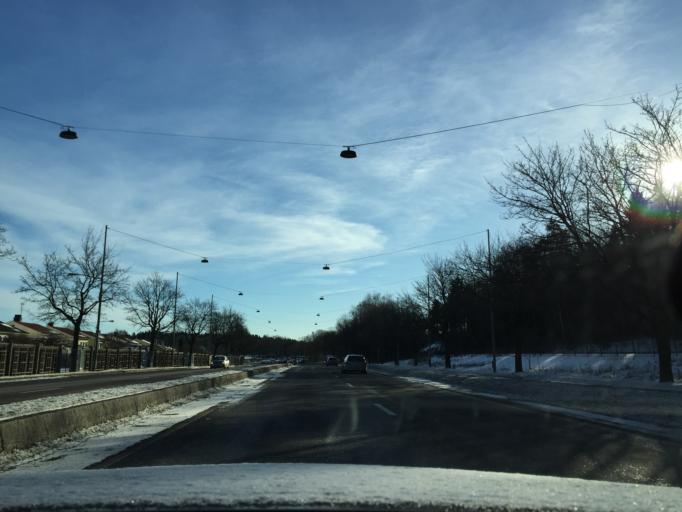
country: SE
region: Stockholm
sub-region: Stockholms Kommun
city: Bromma
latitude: 59.3442
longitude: 17.9015
